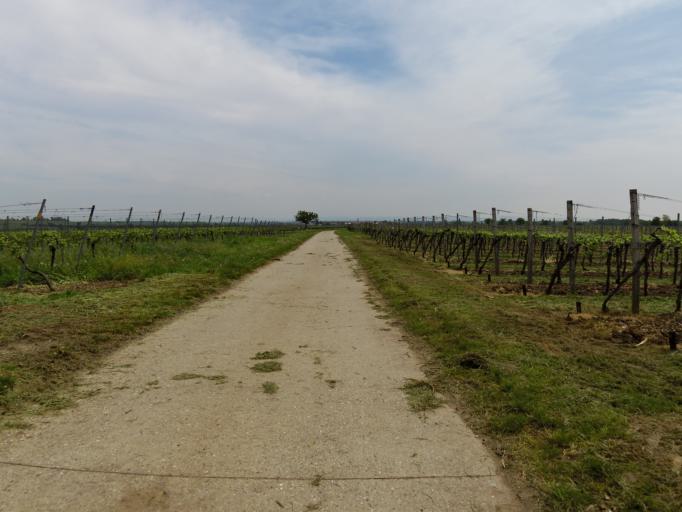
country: DE
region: Rheinland-Pfalz
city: Kallstadt
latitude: 49.4884
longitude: 8.1934
